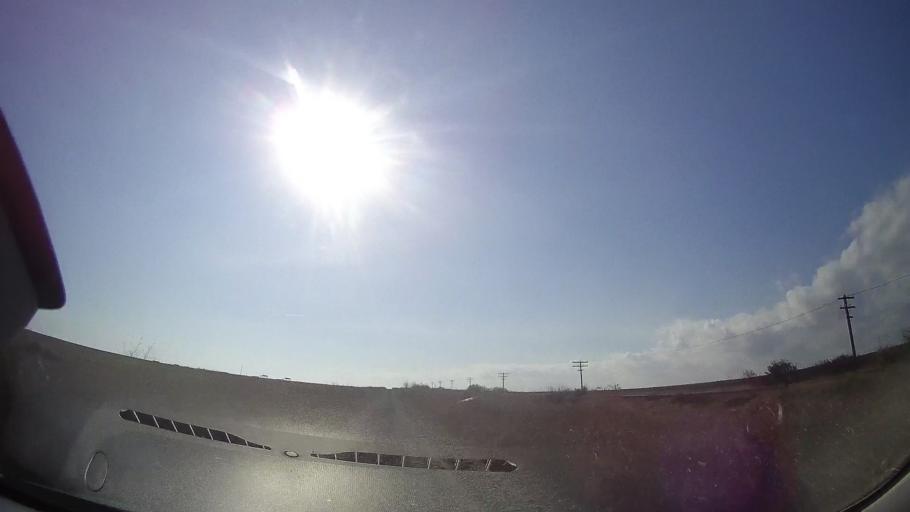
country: RO
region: Constanta
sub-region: Comuna Costinesti
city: Schitu
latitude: 43.9211
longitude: 28.6307
